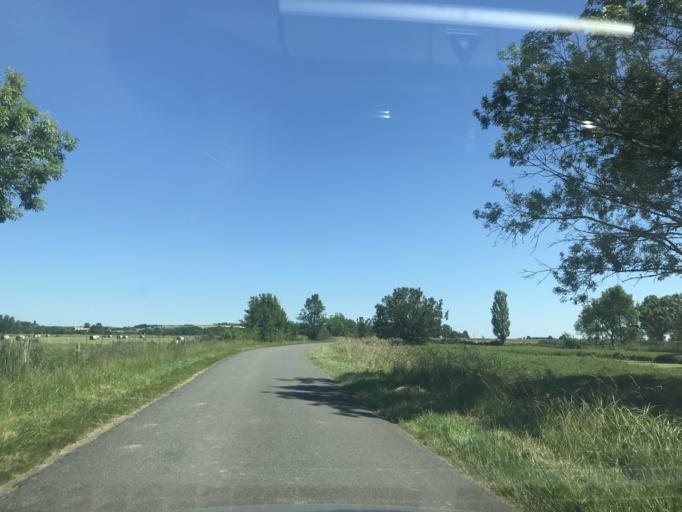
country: FR
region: Poitou-Charentes
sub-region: Departement de la Charente-Maritime
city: Mortagne-sur-Gironde
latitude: 45.4325
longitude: -0.7514
